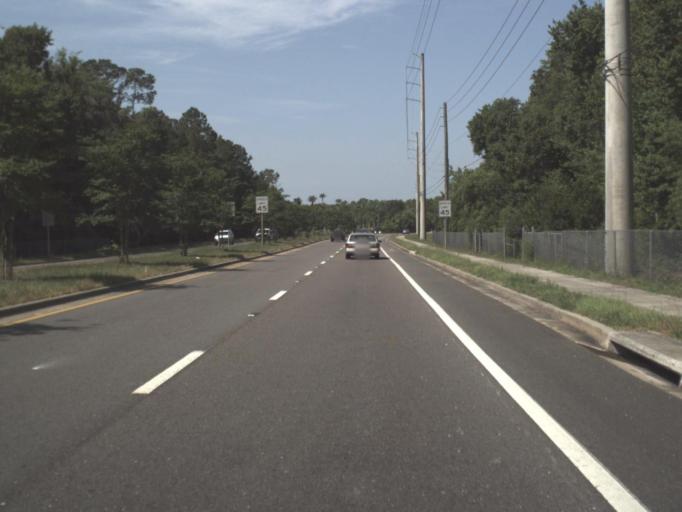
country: US
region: Florida
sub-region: Saint Johns County
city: Saint Augustine Shores
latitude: 29.8168
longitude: -81.3867
